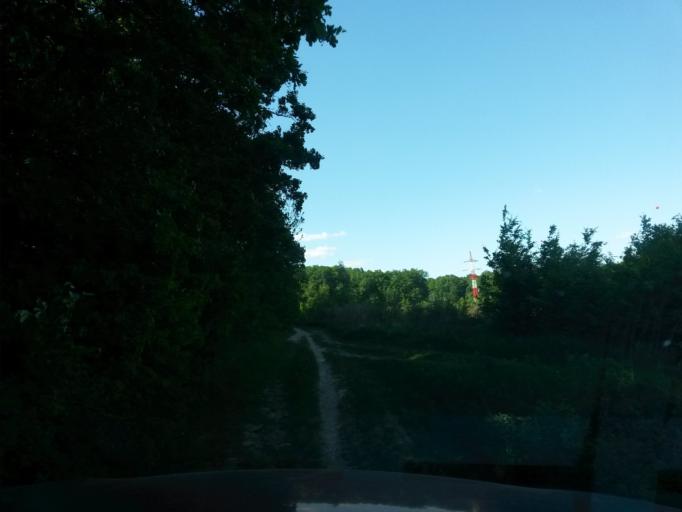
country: SK
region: Kosicky
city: Kosice
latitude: 48.6893
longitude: 21.1820
